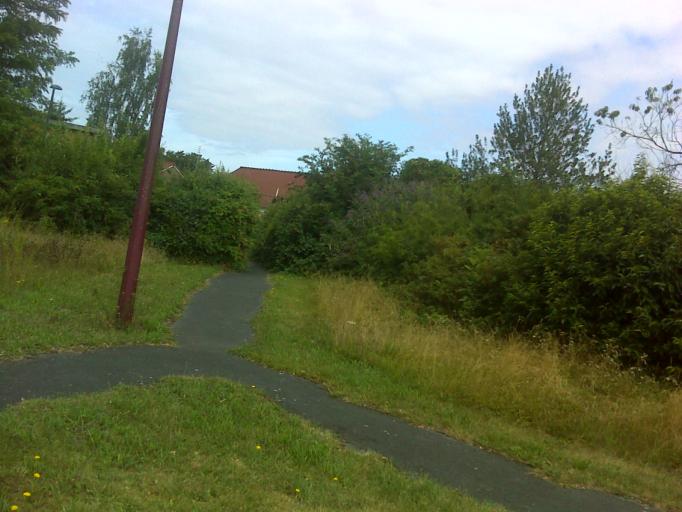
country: FR
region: Nord-Pas-de-Calais
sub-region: Departement du Nord
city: Conde-sur-l'Escaut
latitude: 50.4586
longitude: 3.5944
